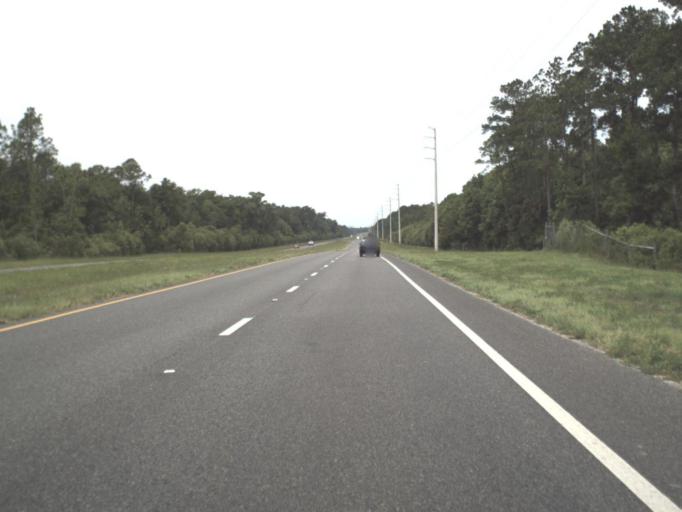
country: US
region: Florida
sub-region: Putnam County
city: Palatka
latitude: 29.6301
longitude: -81.7510
